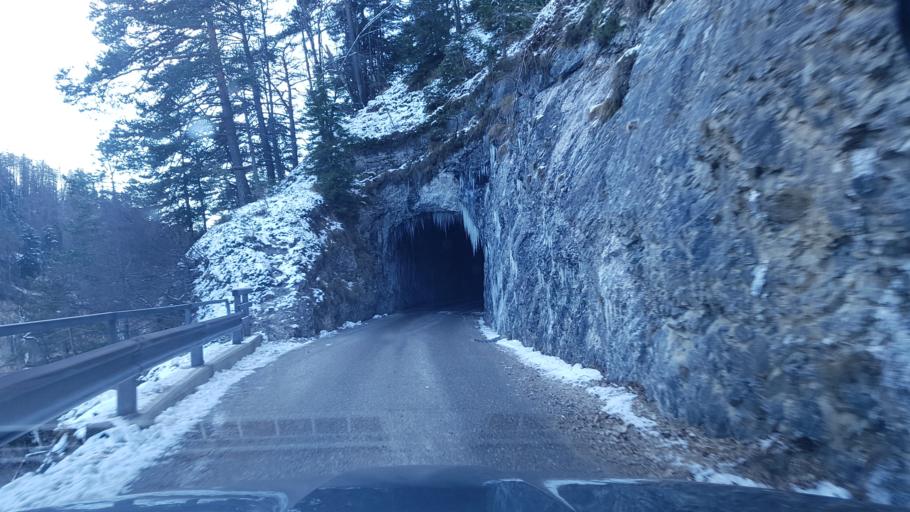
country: AT
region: Salzburg
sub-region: Politischer Bezirk Salzburg-Umgebung
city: Ebenau
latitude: 47.7751
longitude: 13.1993
